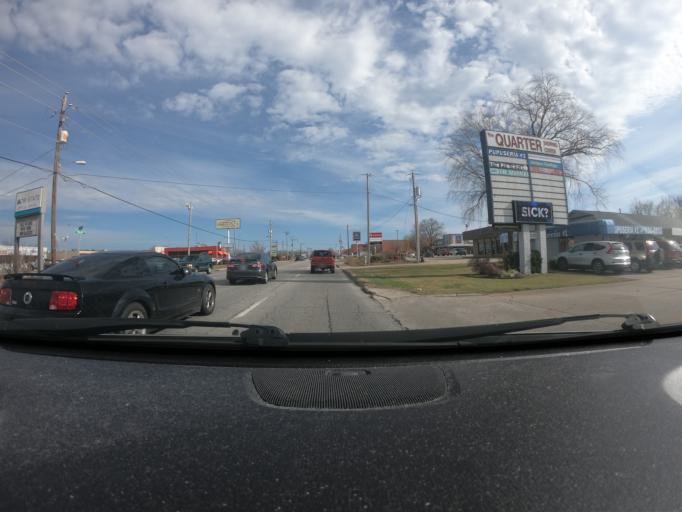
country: US
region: Arkansas
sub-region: Benton County
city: Rogers
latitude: 36.3338
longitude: -94.1376
